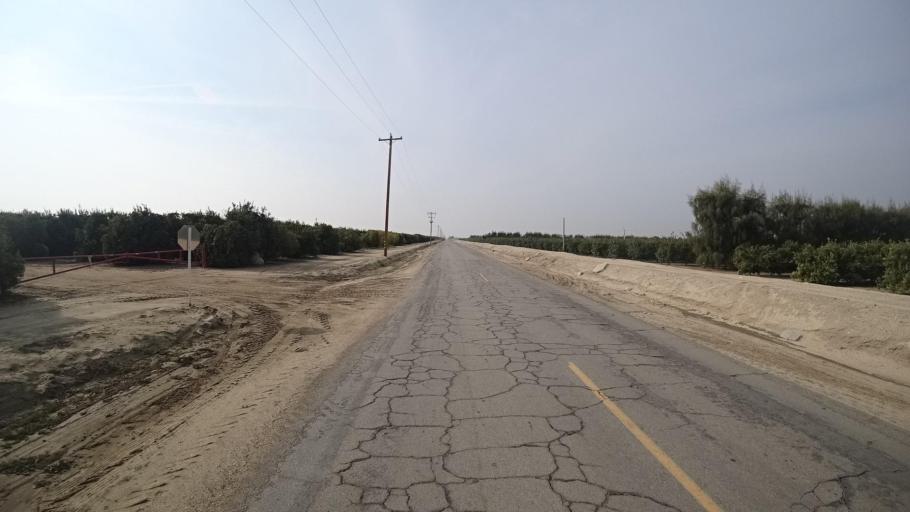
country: US
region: California
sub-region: Kern County
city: Arvin
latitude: 35.1511
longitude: -118.8277
